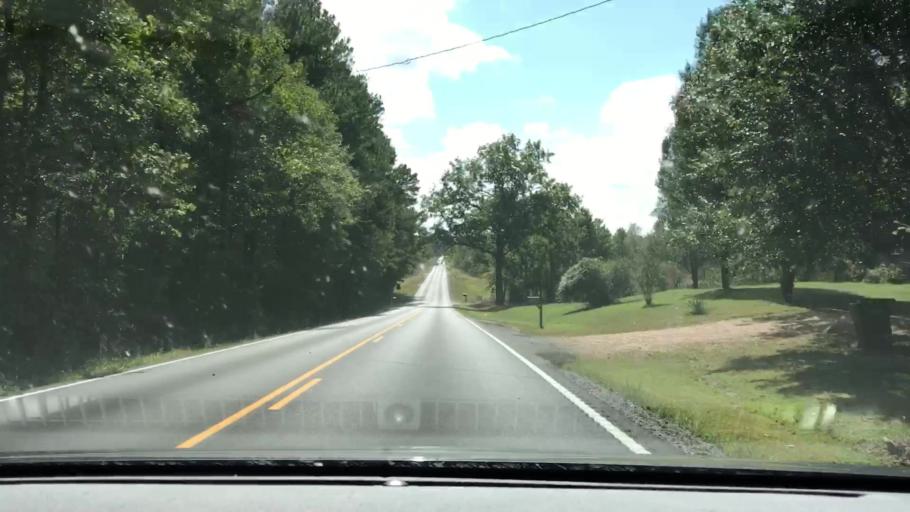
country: US
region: Kentucky
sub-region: Graves County
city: Mayfield
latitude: 36.8668
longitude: -88.5737
